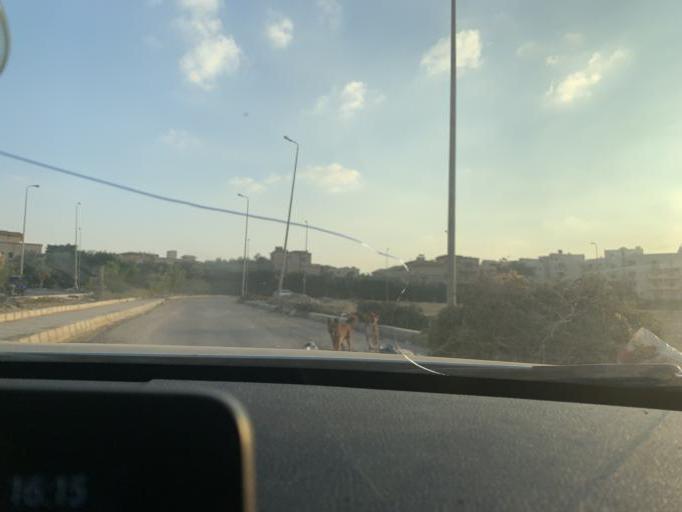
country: EG
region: Muhafazat al Qalyubiyah
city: Al Khankah
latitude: 30.0196
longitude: 31.4818
